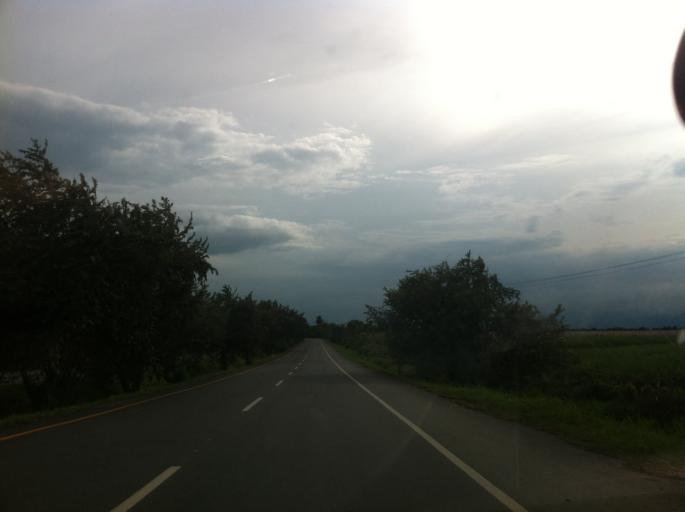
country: CO
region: Valle del Cauca
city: Palmira
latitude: 3.5697
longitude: -76.3315
